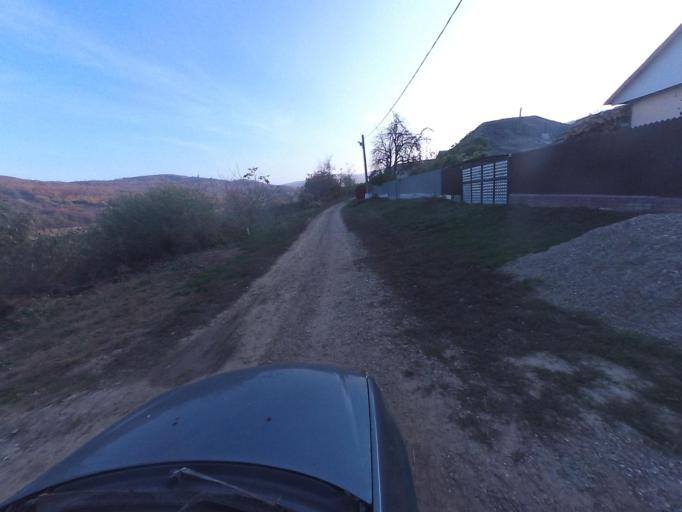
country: RO
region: Vaslui
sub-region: Comuna Bacesti
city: Bacesti
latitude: 46.7982
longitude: 27.2254
